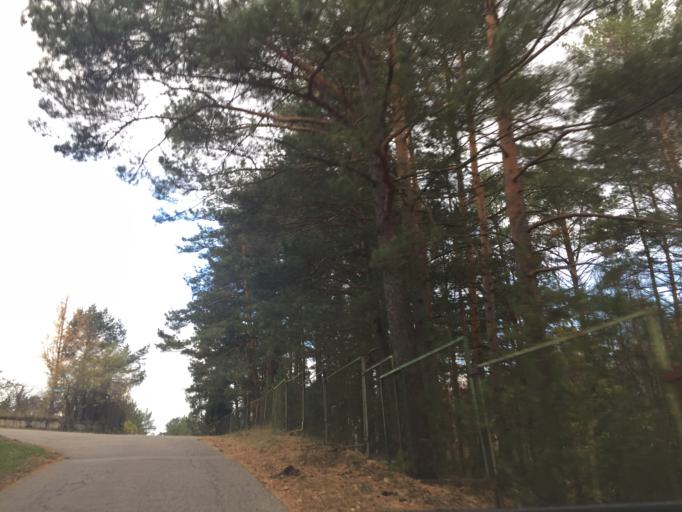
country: LV
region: Carnikava
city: Carnikava
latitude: 57.1514
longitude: 24.2892
